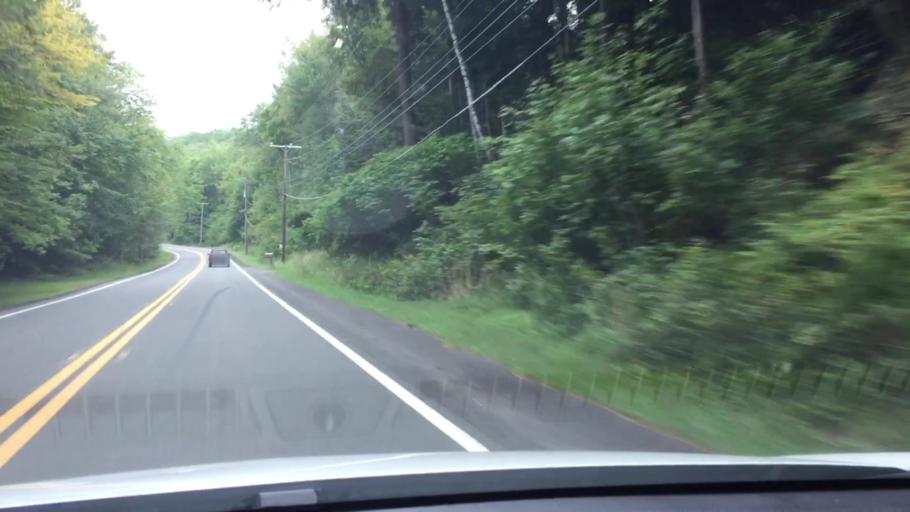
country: US
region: Massachusetts
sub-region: Berkshire County
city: Hinsdale
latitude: 42.3825
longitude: -73.1224
